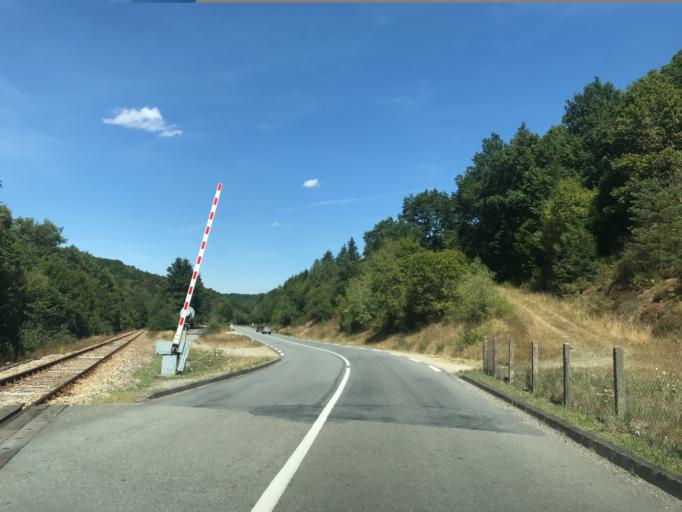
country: FR
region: Limousin
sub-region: Departement de la Creuse
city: Felletin
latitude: 45.9048
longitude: 2.1878
